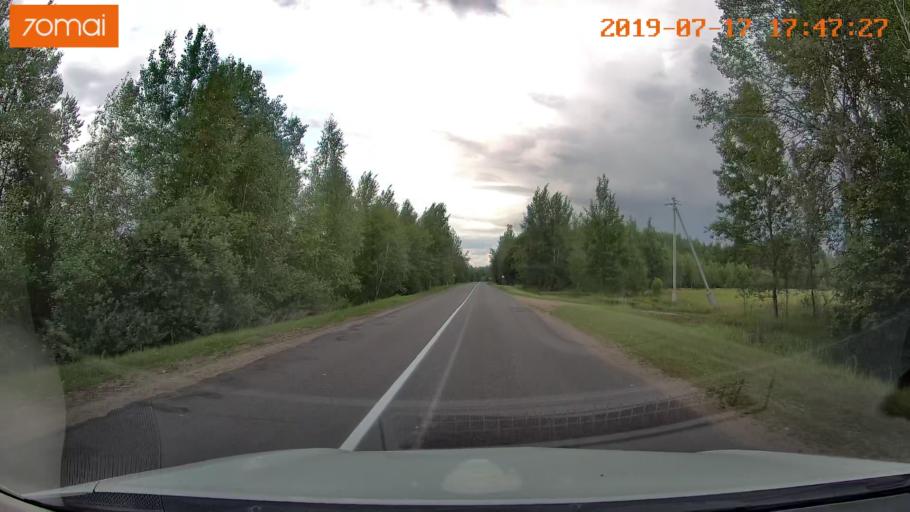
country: BY
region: Mogilev
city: Hlusha
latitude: 53.1108
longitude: 28.8289
